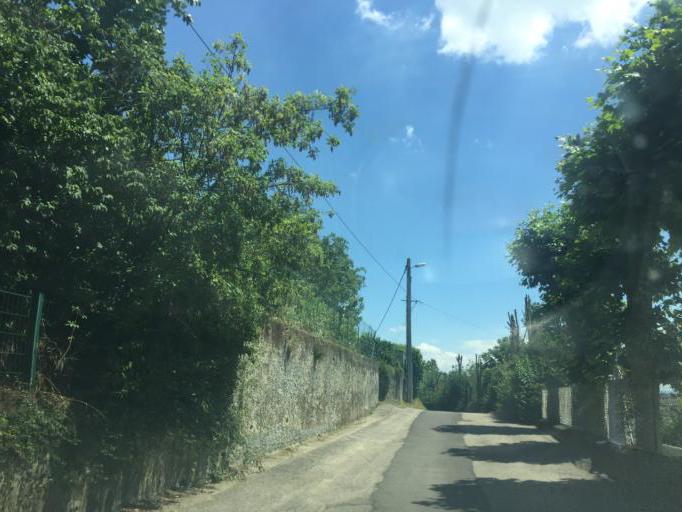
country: FR
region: Rhone-Alpes
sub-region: Departement de l'Ain
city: Beynost
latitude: 45.8406
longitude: 4.9960
